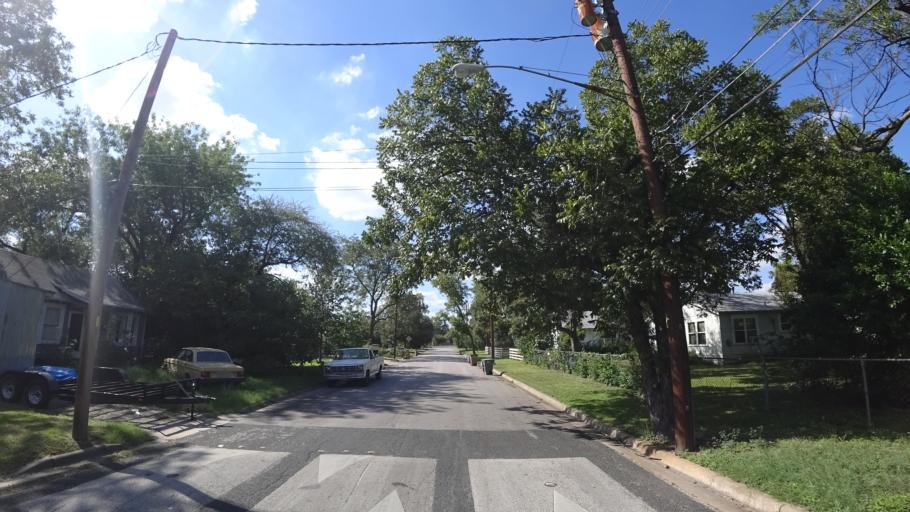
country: US
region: Texas
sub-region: Travis County
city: Austin
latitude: 30.3123
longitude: -97.7136
